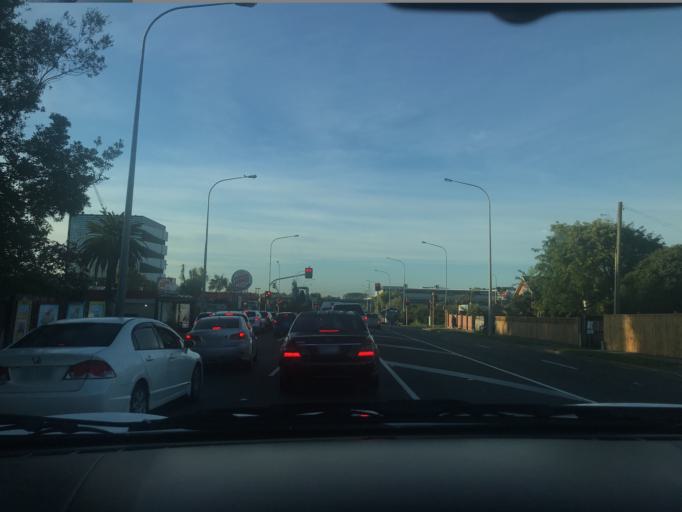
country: NZ
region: Auckland
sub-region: Auckland
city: Tamaki
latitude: -36.9126
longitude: 174.8384
